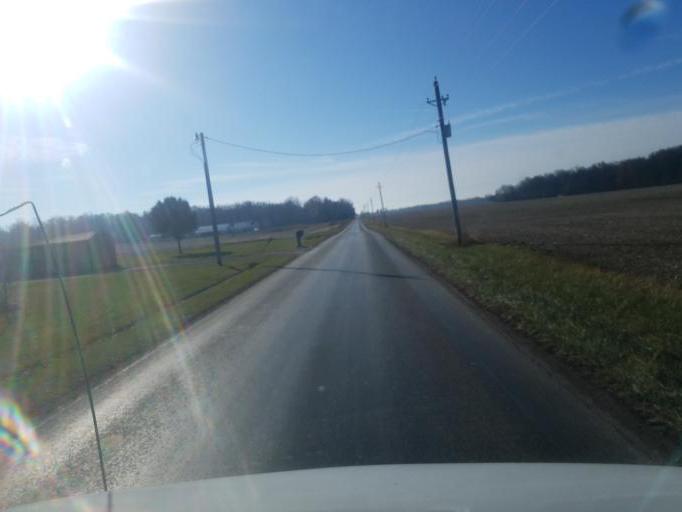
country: US
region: Indiana
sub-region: Adams County
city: Geneva
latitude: 40.5586
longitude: -84.9919
